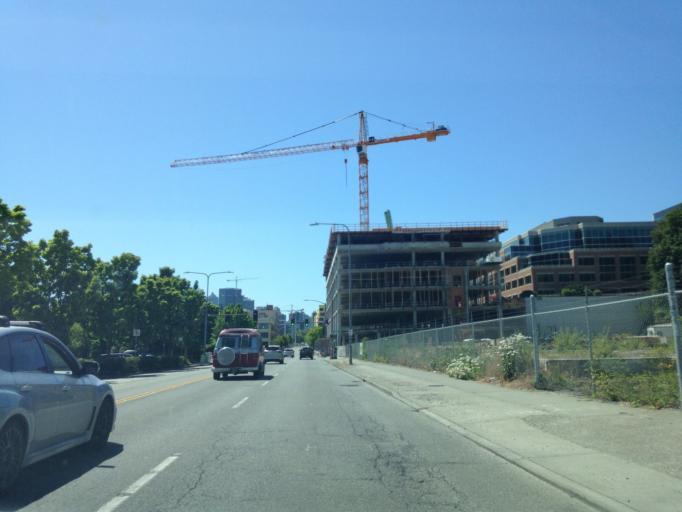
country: US
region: Washington
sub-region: King County
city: Seattle
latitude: 47.6307
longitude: -122.3411
